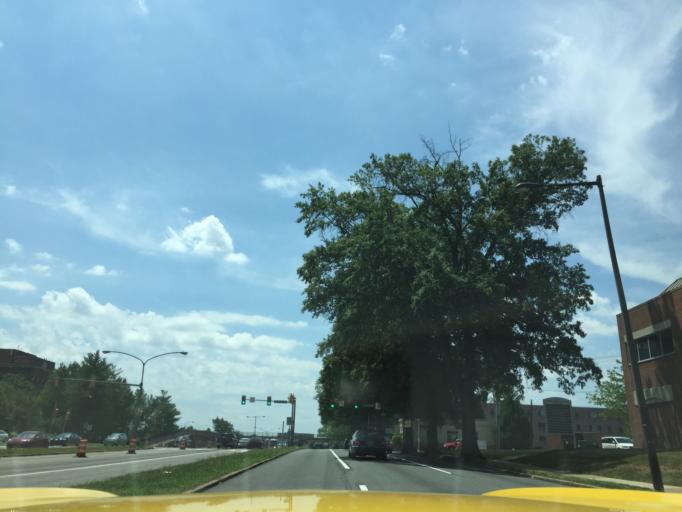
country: US
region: Pennsylvania
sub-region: Montgomery County
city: Rockledge
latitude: 40.0633
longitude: -75.0427
